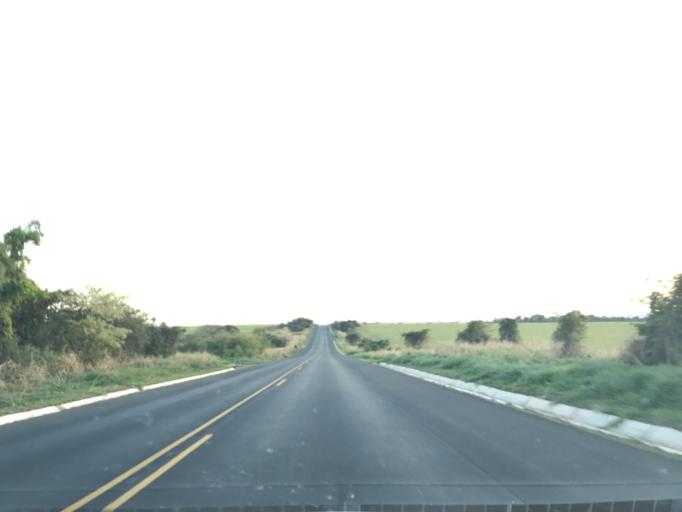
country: BR
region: Sao Paulo
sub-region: Pirapozinho
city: Pirapozinho
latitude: -22.4069
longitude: -51.6272
